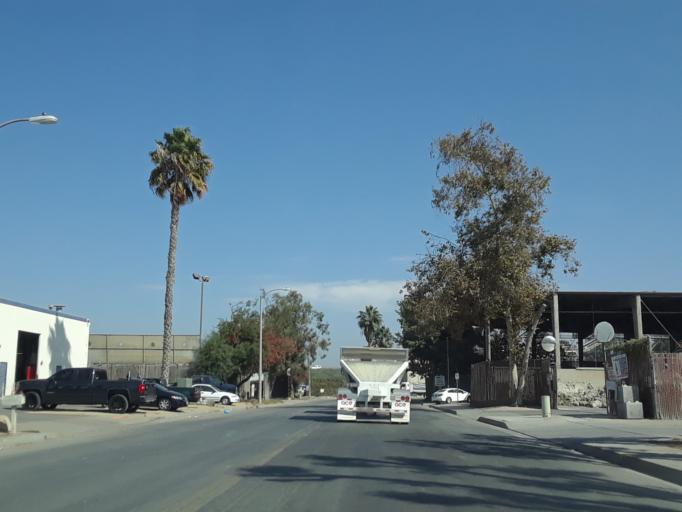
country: US
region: California
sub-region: Orange County
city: Irvine
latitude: 33.6963
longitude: -117.8216
